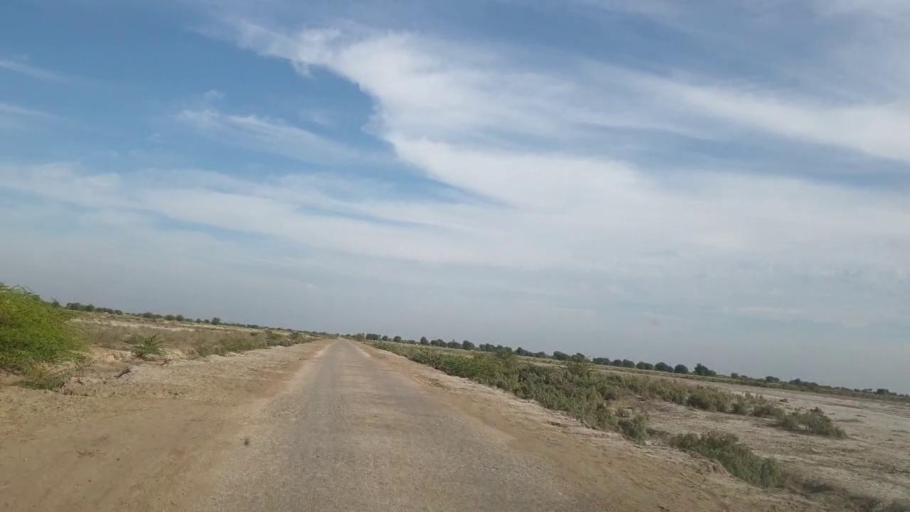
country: PK
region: Sindh
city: Pithoro
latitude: 25.6377
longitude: 69.3858
